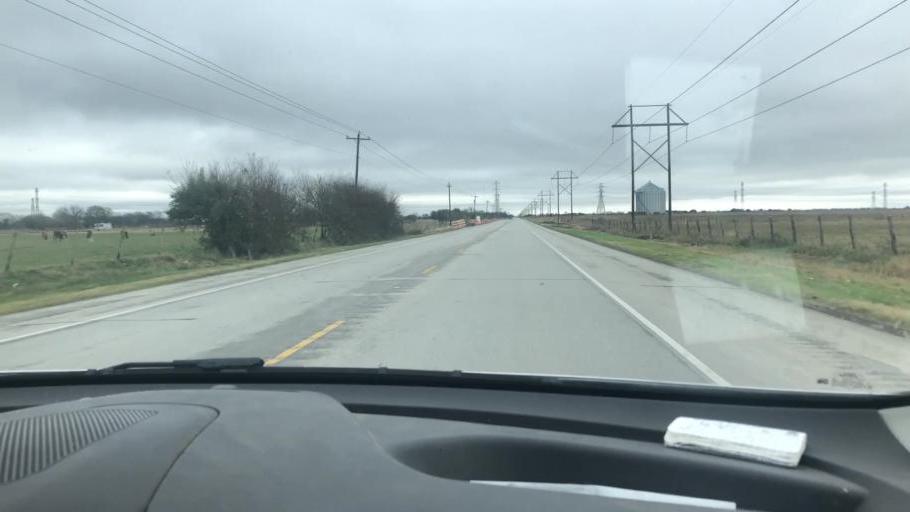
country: US
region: Texas
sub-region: Wharton County
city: Boling
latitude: 29.1828
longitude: -96.0096
